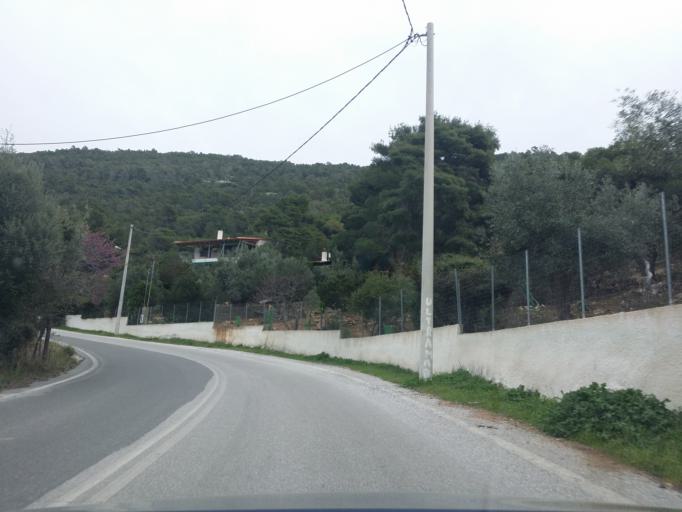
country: GR
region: Central Greece
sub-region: Nomos Voiotias
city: Kaparellion
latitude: 38.1473
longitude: 23.2353
